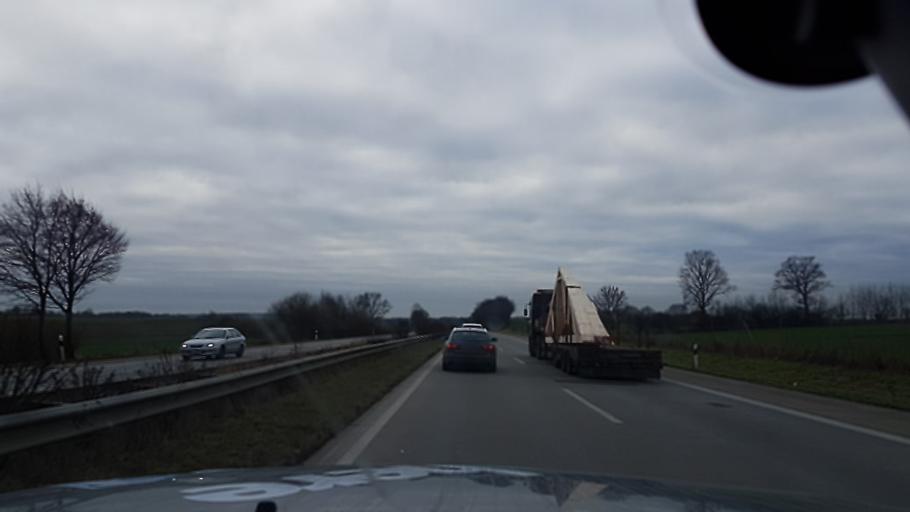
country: DE
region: Schleswig-Holstein
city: Ratekau
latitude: 53.9830
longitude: 10.7332
